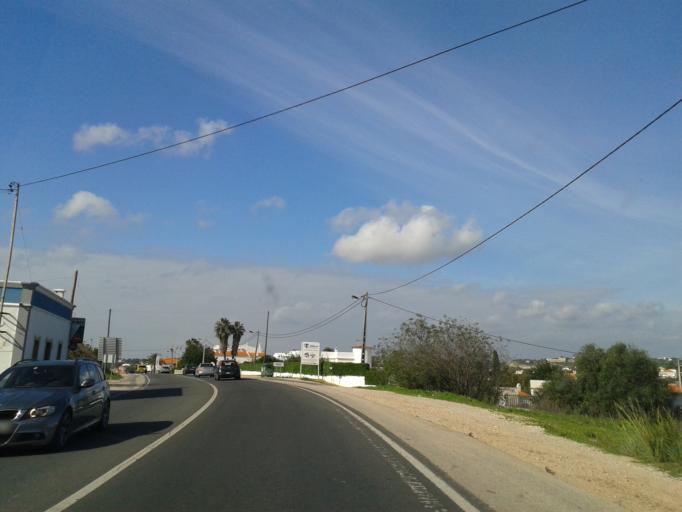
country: PT
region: Faro
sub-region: Faro
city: Santa Barbara de Nexe
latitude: 37.0785
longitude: -7.9912
